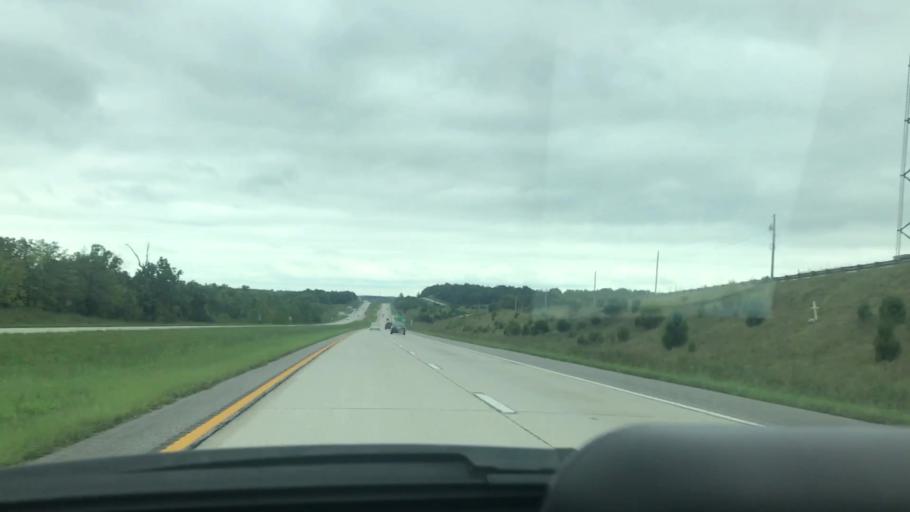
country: US
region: Missouri
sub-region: Greene County
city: Fair Grove
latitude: 37.5099
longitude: -93.1388
